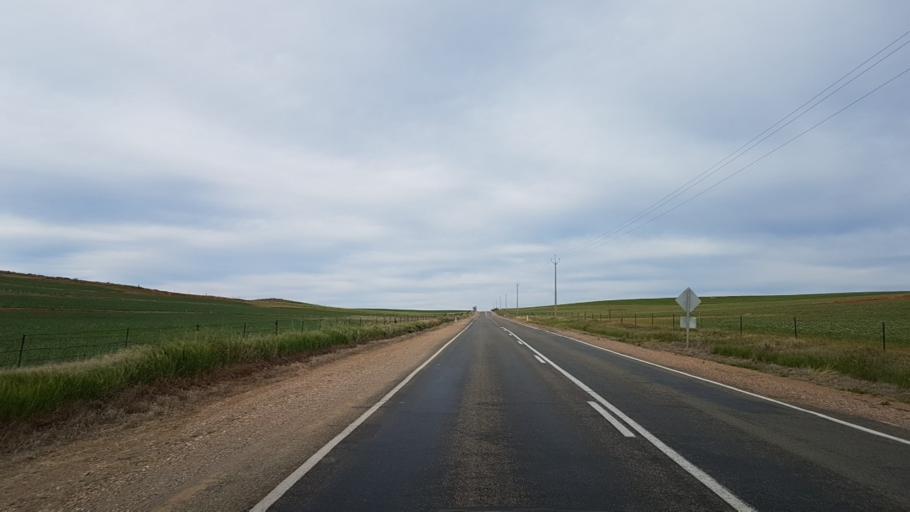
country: AU
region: South Australia
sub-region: Northern Areas
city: Jamestown
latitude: -33.1974
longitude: 138.4452
